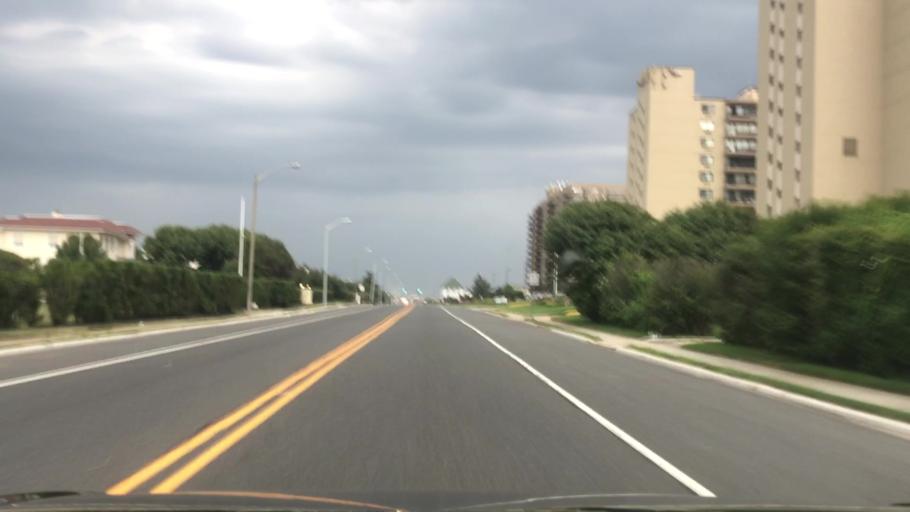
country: US
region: New Jersey
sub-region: Monmouth County
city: Monmouth Beach
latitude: 40.3280
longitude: -73.9755
